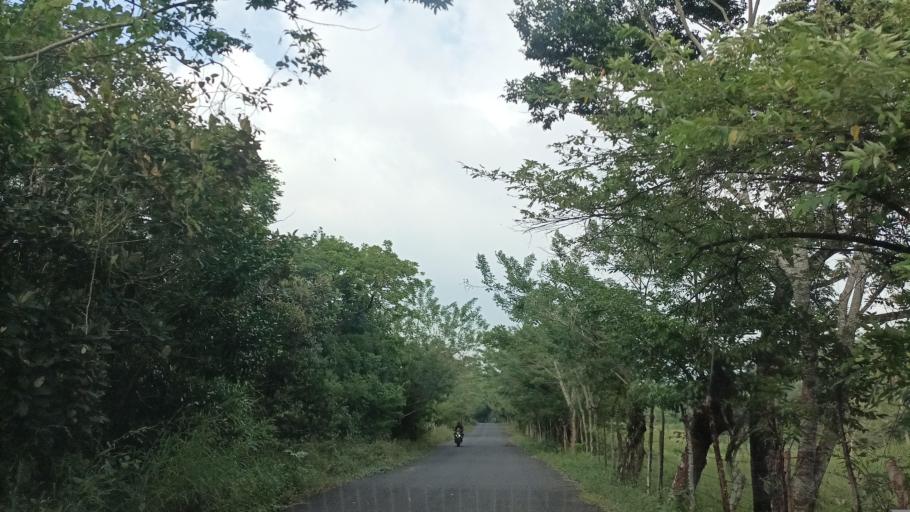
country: MX
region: Veracruz
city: Allende
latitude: 18.1196
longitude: -94.2872
